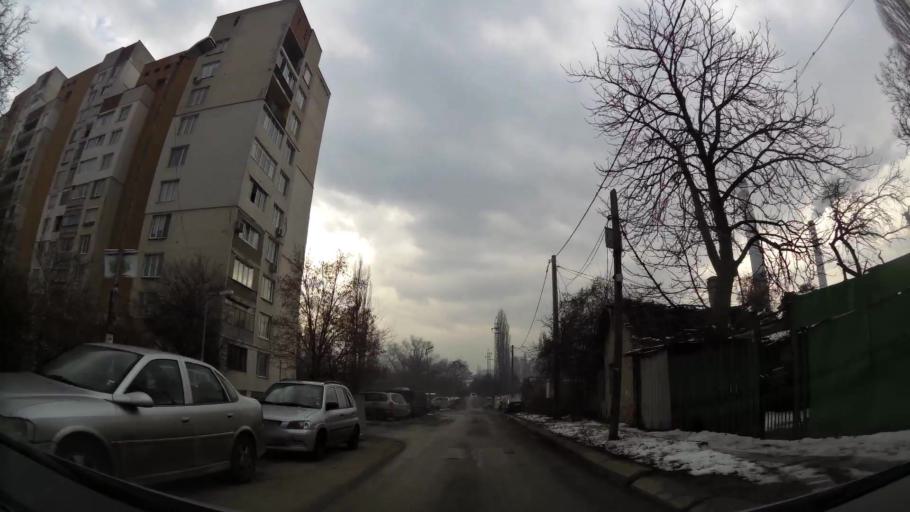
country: BG
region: Sofia-Capital
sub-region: Stolichna Obshtina
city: Sofia
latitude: 42.6903
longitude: 23.2847
